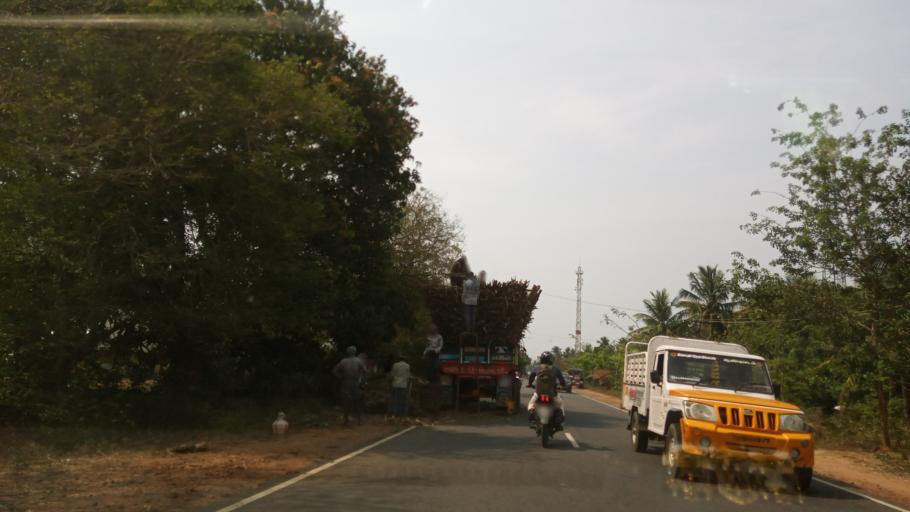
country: IN
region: Tamil Nadu
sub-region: Cuddalore
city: Srimushnam
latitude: 11.4049
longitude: 79.3577
